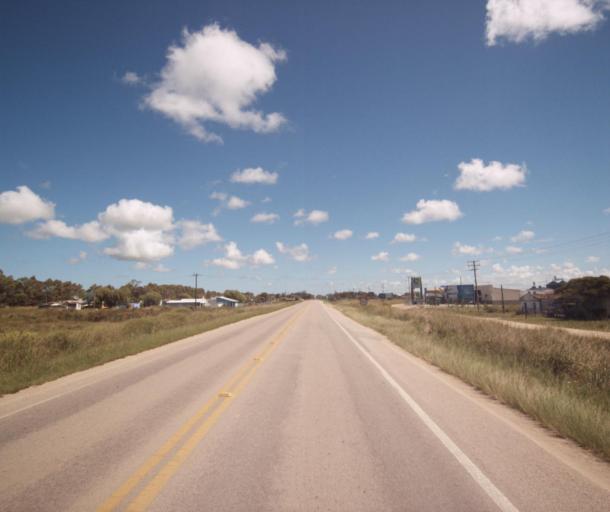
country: BR
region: Rio Grande do Sul
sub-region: Santa Vitoria Do Palmar
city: Santa Vitoria do Palmar
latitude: -33.5283
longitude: -53.3432
